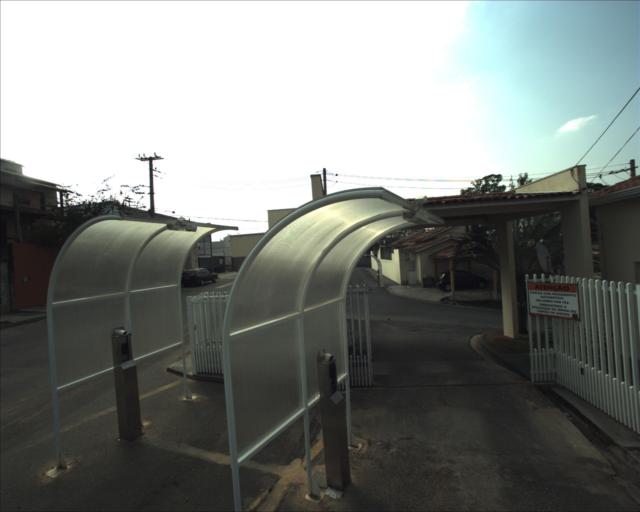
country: BR
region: Sao Paulo
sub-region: Sorocaba
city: Sorocaba
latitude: -23.4463
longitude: -47.4957
